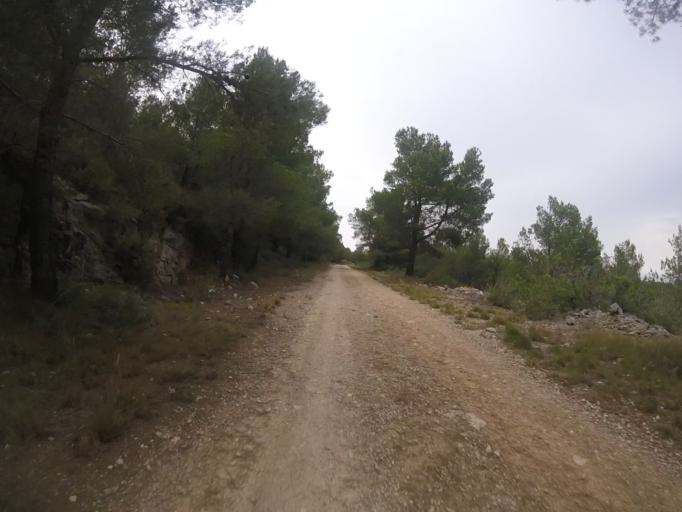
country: ES
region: Valencia
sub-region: Provincia de Castello
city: Alcoceber
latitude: 40.2808
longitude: 0.2833
